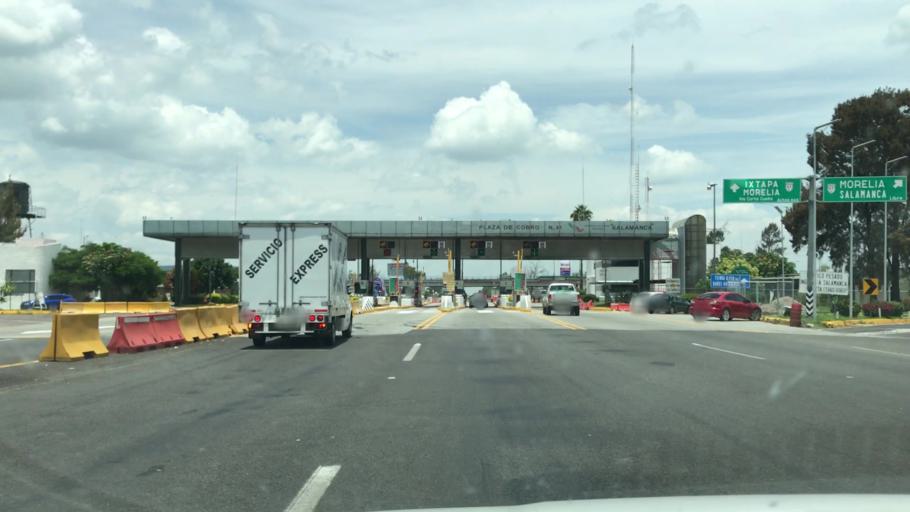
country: MX
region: Guanajuato
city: Salamanca
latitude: 20.5986
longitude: -101.1819
